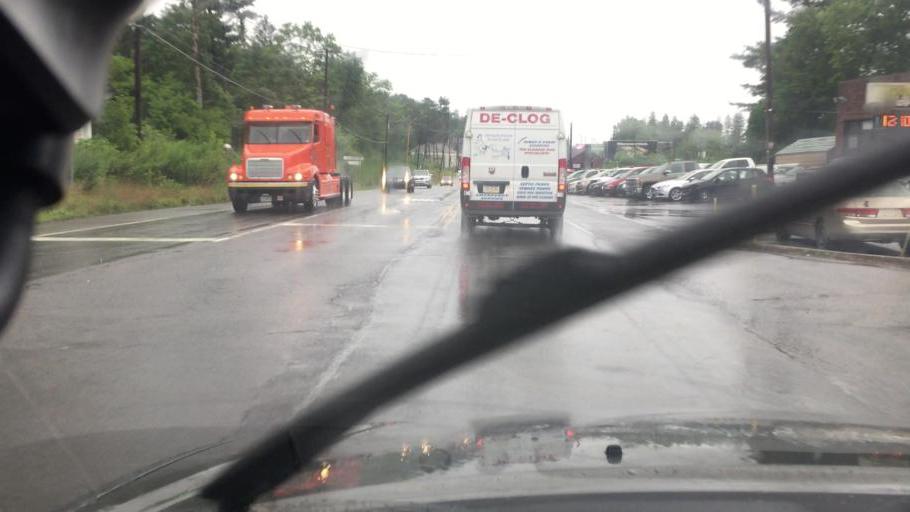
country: US
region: Pennsylvania
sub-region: Monroe County
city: Tannersville
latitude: 41.0049
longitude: -75.2796
